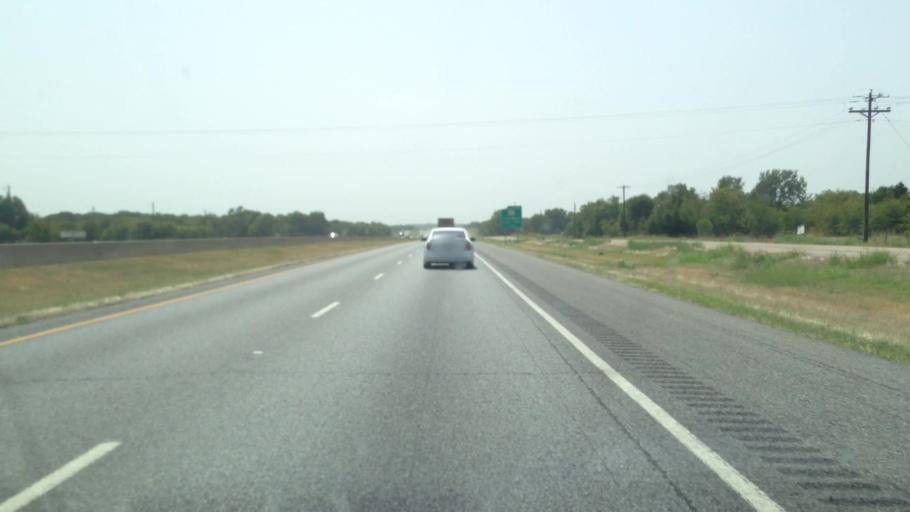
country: US
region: Texas
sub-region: Hunt County
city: Commerce
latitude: 33.1317
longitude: -95.9225
